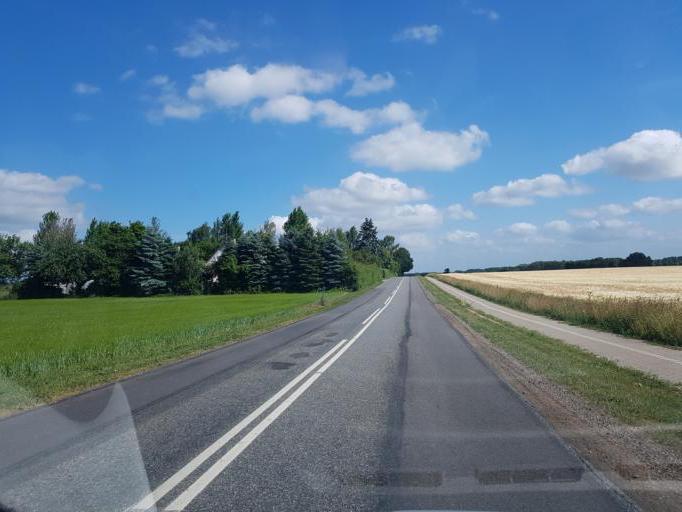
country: DK
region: Zealand
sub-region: Lejre Kommune
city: Osted
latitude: 55.5815
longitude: 11.9681
